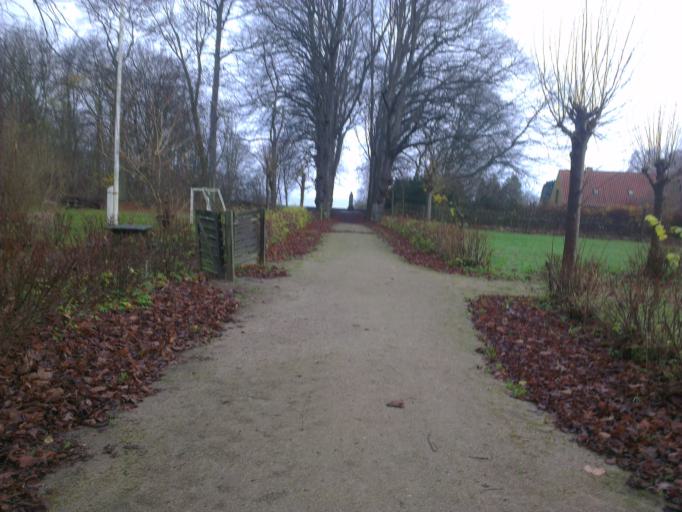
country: DK
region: Capital Region
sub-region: Frederikssund Kommune
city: Jaegerspris
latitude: 55.8626
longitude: 11.9898
